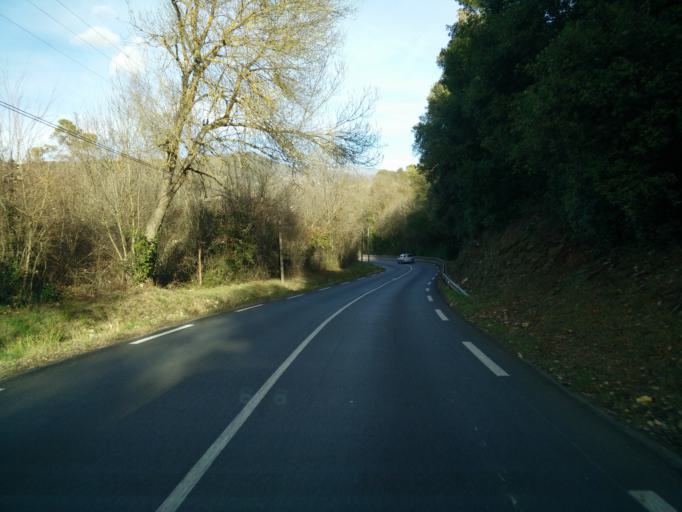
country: FR
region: Provence-Alpes-Cote d'Azur
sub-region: Departement des Alpes-Maritimes
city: Le Tignet
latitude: 43.6135
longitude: 6.8201
